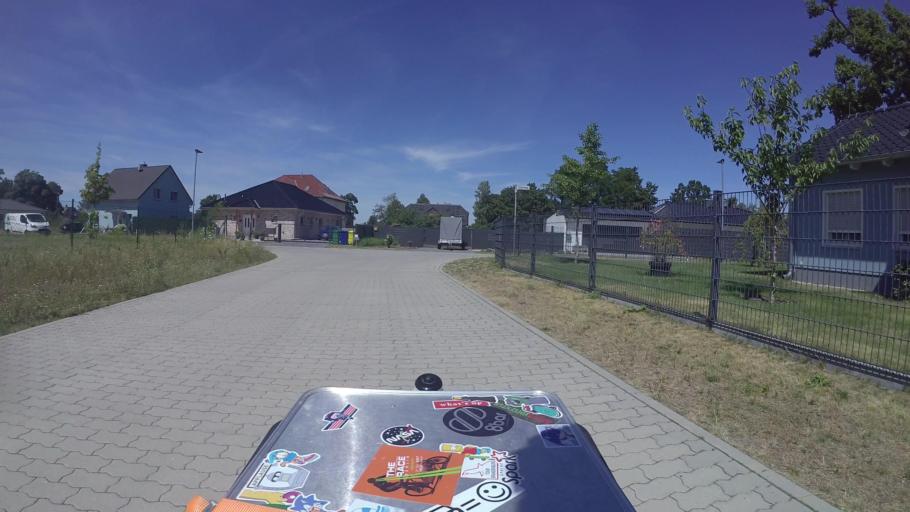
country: DE
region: Brandenburg
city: Sperenberg
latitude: 52.1648
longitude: 13.3716
